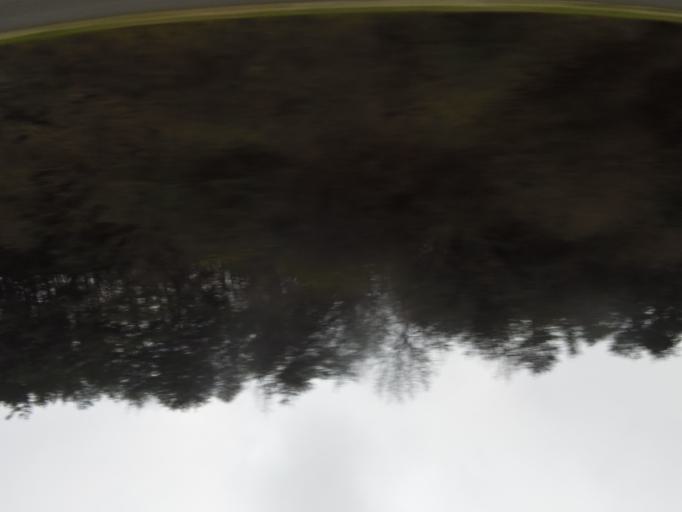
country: US
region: Alabama
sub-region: Jefferson County
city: Morris
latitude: 33.7385
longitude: -86.8260
